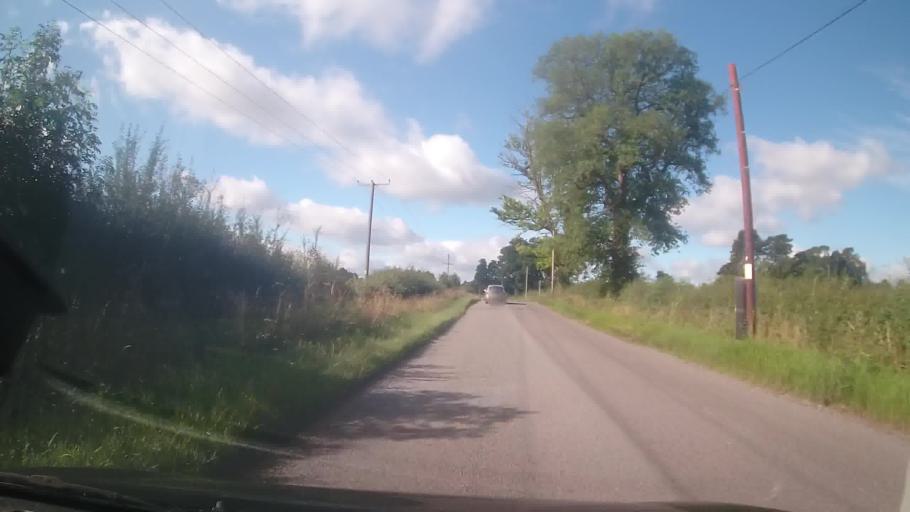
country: GB
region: England
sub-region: Shropshire
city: Bicton
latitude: 52.7568
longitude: -2.8277
